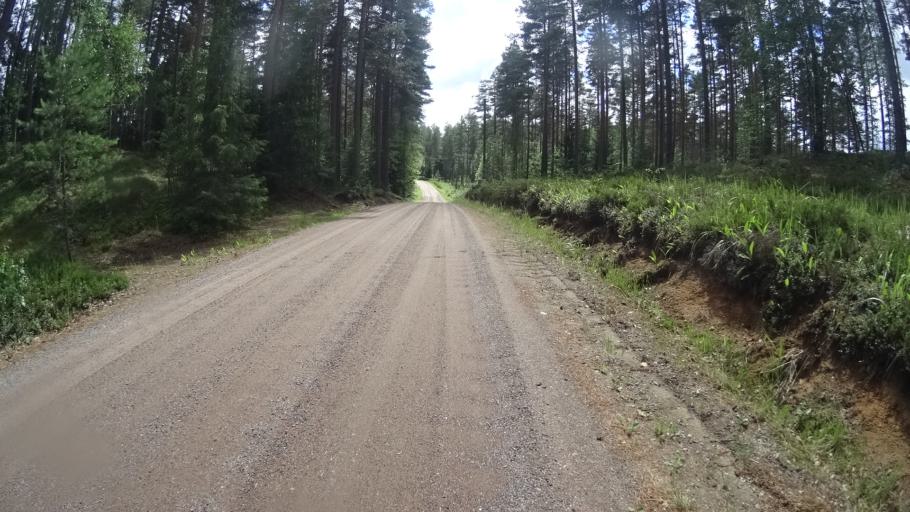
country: FI
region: Uusimaa
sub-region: Helsinki
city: Karkkila
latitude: 60.6042
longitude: 24.1827
